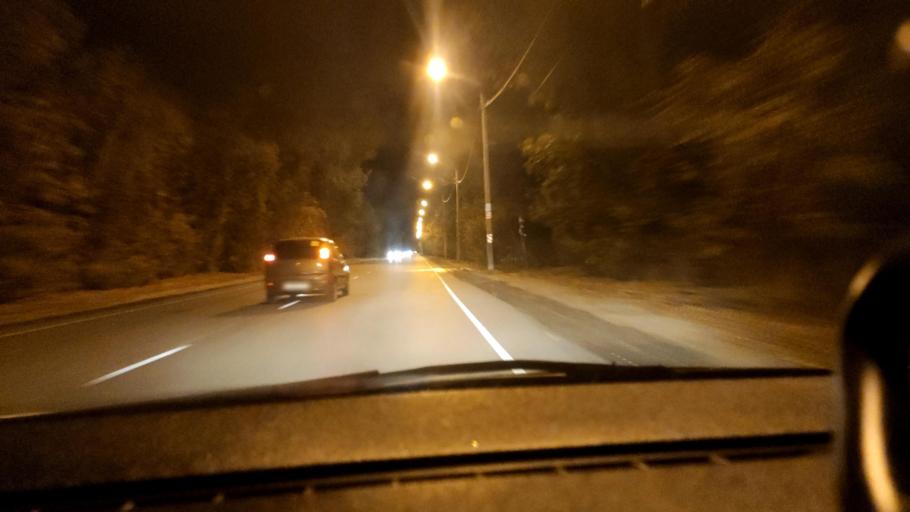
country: RU
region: Voronezj
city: Voronezh
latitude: 51.5995
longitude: 39.1770
